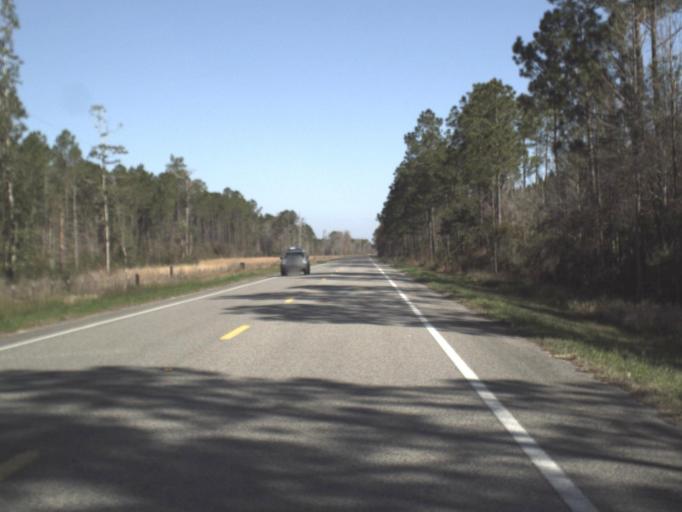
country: US
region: Florida
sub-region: Leon County
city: Woodville
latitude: 30.2454
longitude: -84.0427
